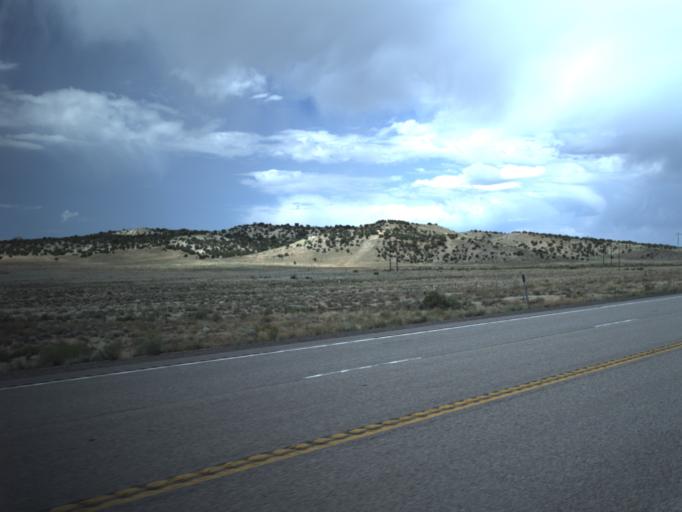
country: US
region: Utah
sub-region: Carbon County
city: Wellington
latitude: 39.5435
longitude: -110.6146
